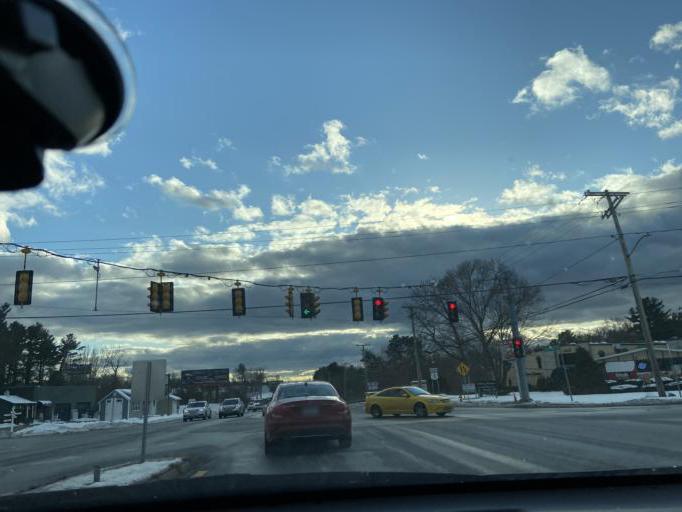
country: US
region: Massachusetts
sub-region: Norfolk County
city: Walpole
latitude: 42.1236
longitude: -71.2309
